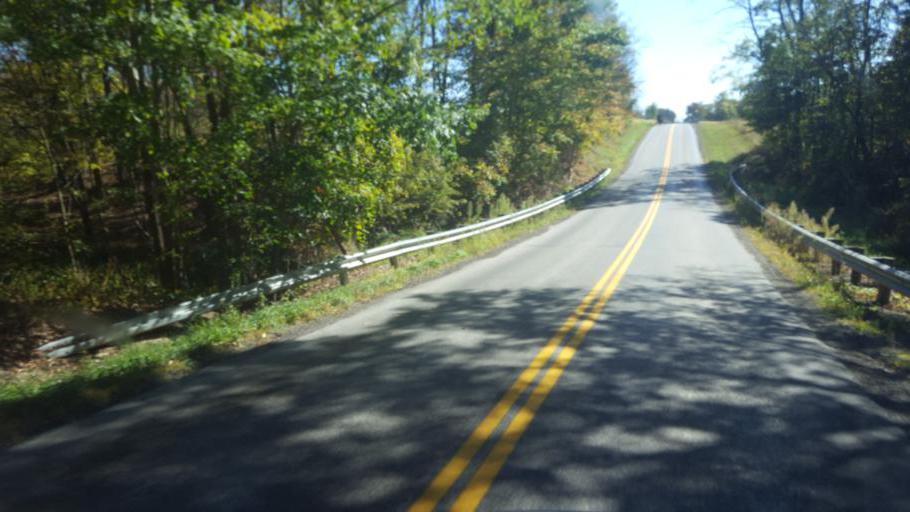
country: US
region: Ohio
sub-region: Wayne County
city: West Salem
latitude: 40.9277
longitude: -82.1617
